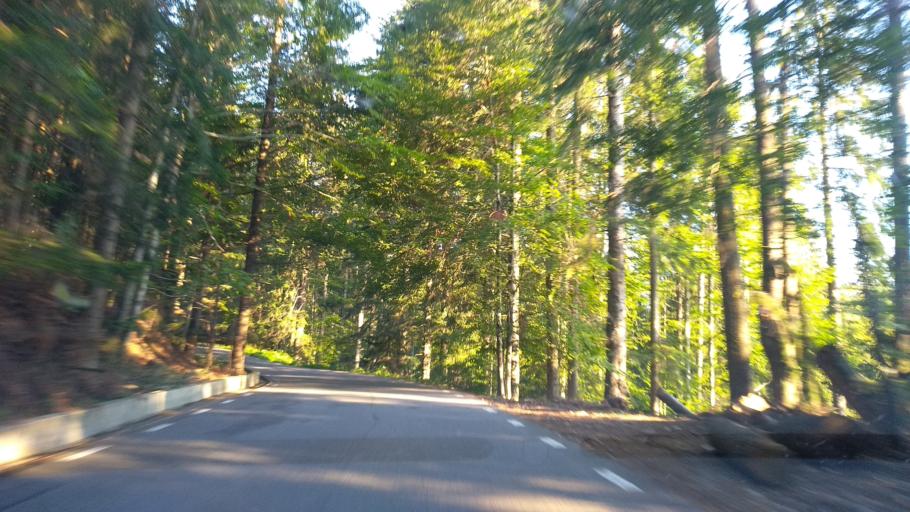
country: RO
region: Prahova
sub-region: Oras Sinaia
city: Sinaia
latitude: 45.3223
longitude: 25.5117
